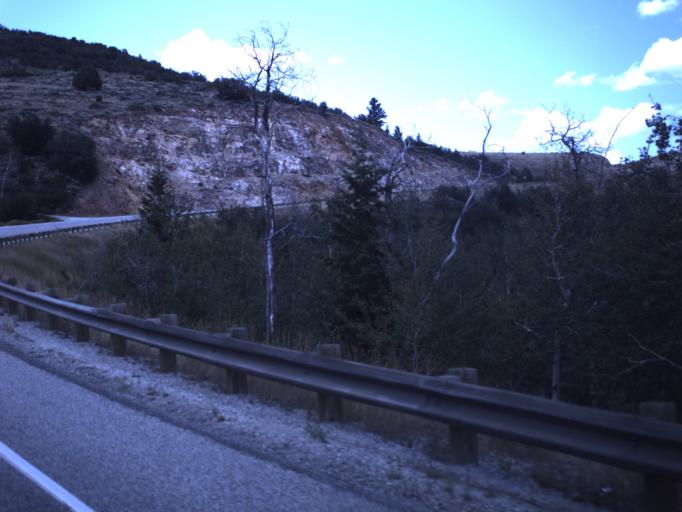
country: US
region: Idaho
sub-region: Bear Lake County
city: Paris
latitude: 41.9257
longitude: -111.4304
